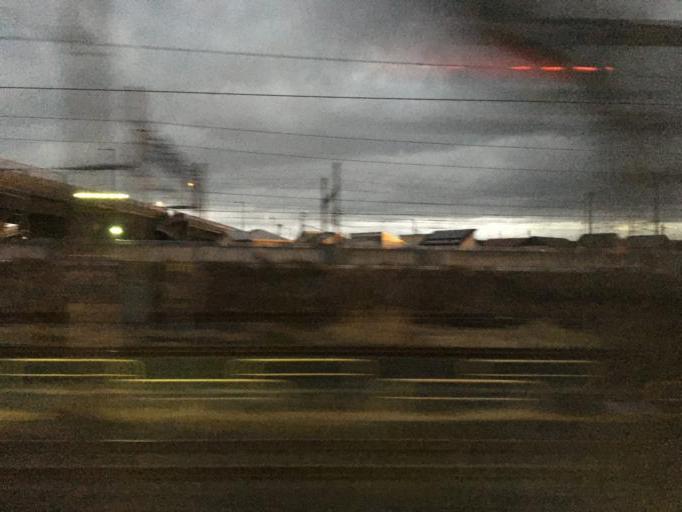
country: JP
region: Aomori
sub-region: Hachinohe Shi
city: Uchimaru
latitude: 40.5150
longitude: 141.4375
